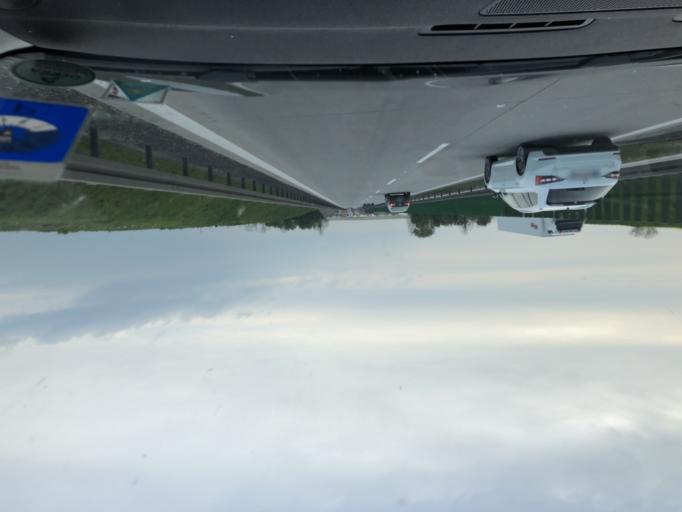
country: PL
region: Lower Silesian Voivodeship
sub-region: Powiat sredzki
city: Udanin
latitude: 51.1048
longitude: 16.4016
